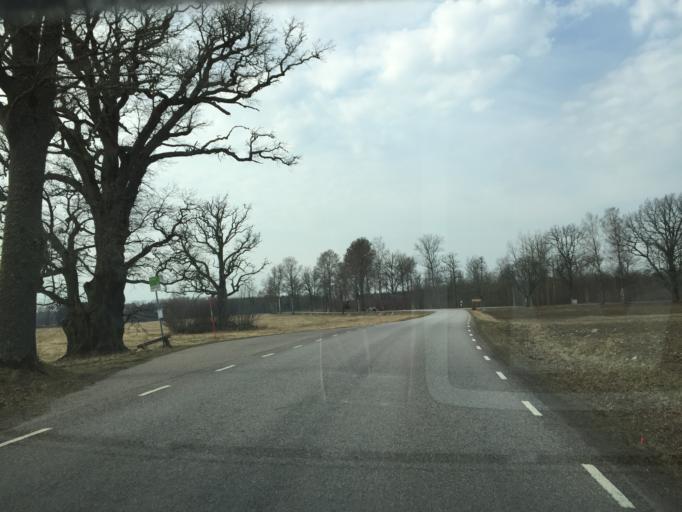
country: SE
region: Soedermanland
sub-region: Vingakers Kommun
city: Vingaker
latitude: 59.0394
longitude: 15.7330
